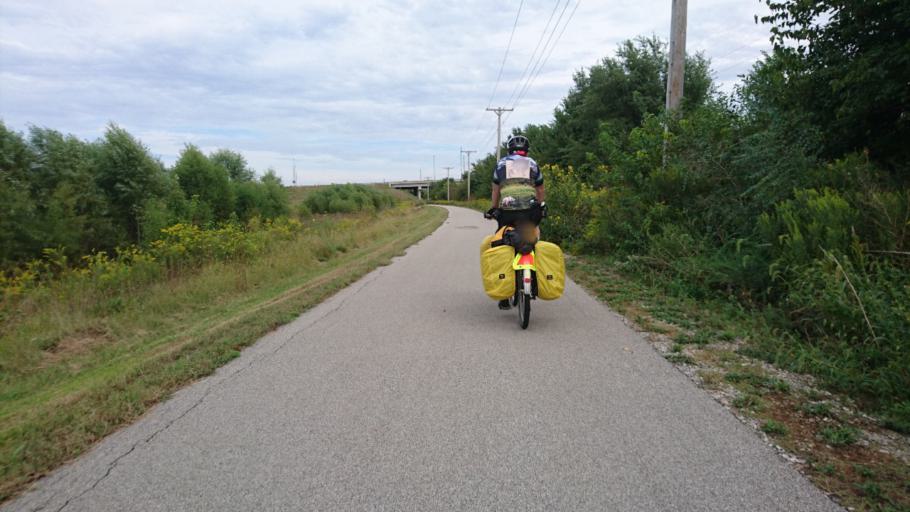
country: US
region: Illinois
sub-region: Sangamon County
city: Jerome
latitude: 39.7429
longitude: -89.6748
